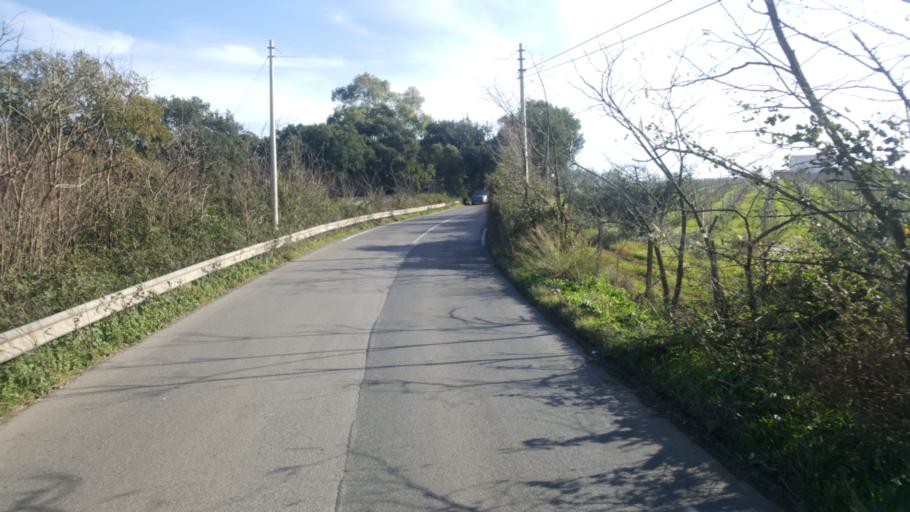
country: IT
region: Latium
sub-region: Citta metropolitana di Roma Capitale
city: Mantiglia di Ardea
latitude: 41.6877
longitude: 12.6072
